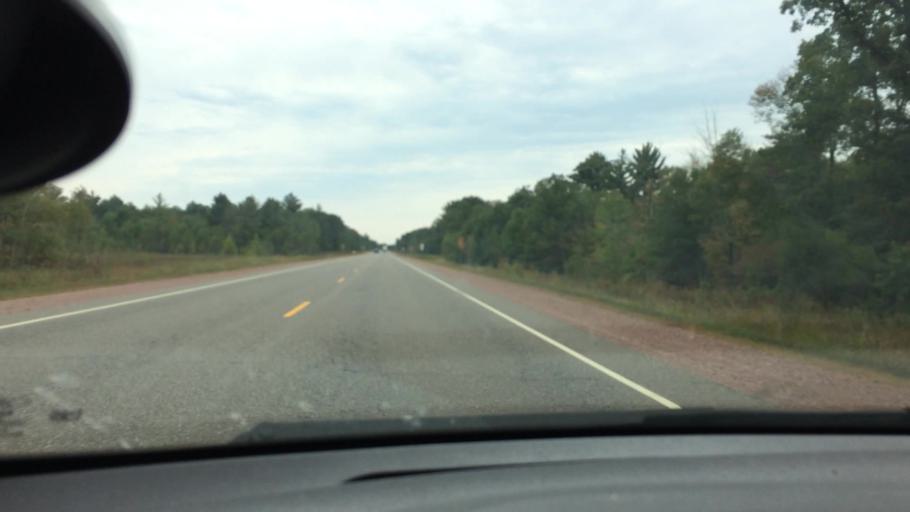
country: US
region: Wisconsin
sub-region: Clark County
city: Neillsville
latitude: 44.5654
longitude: -90.7058
